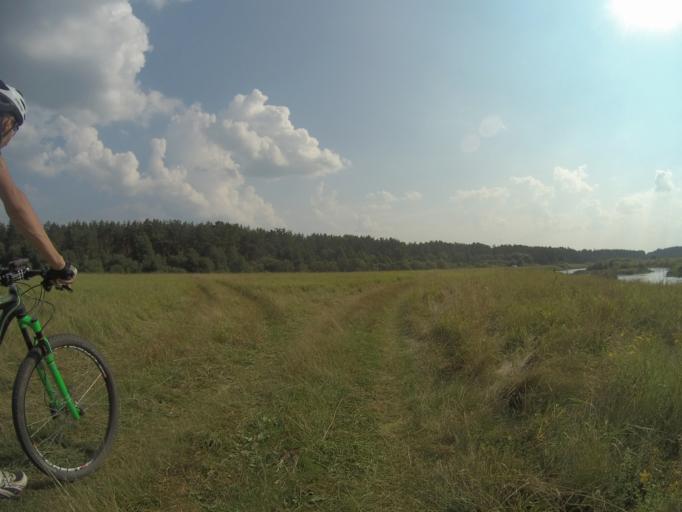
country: RU
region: Vladimir
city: Orgtrud
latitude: 56.3038
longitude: 40.6908
